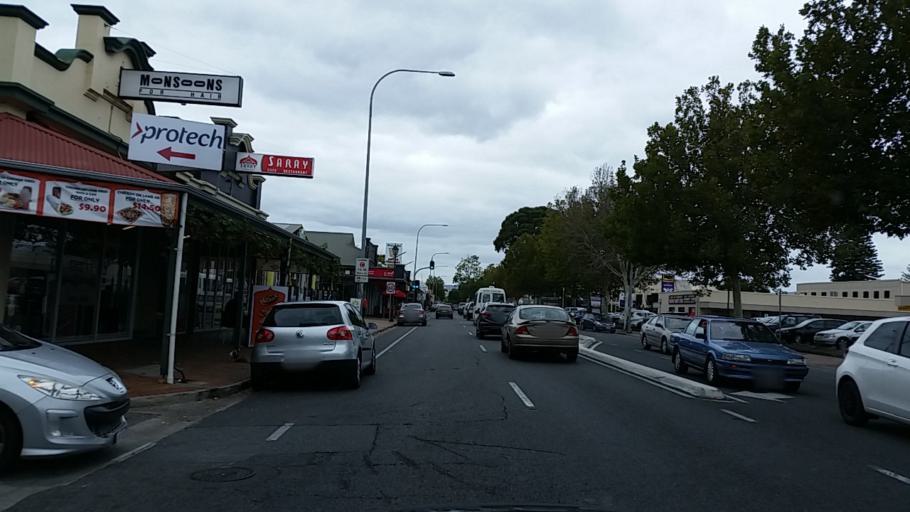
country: AU
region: South Australia
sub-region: City of West Torrens
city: Thebarton
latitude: -34.9241
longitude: 138.5612
